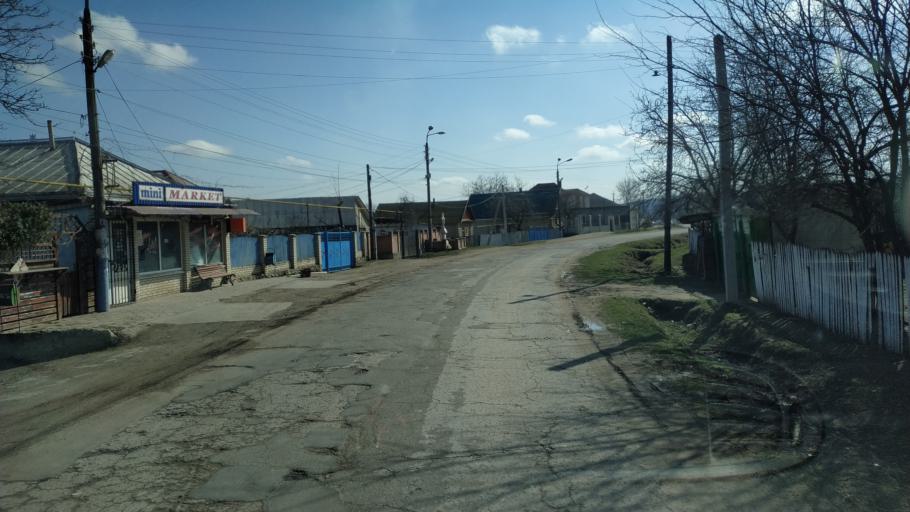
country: MD
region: Hincesti
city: Hincesti
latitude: 46.9639
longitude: 28.6008
